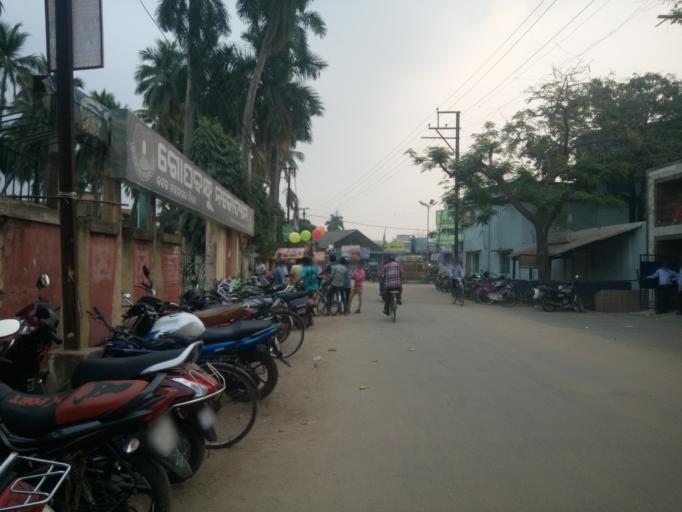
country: IN
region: Odisha
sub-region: Cuttack
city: Cuttack
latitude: 20.4774
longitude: 85.8731
